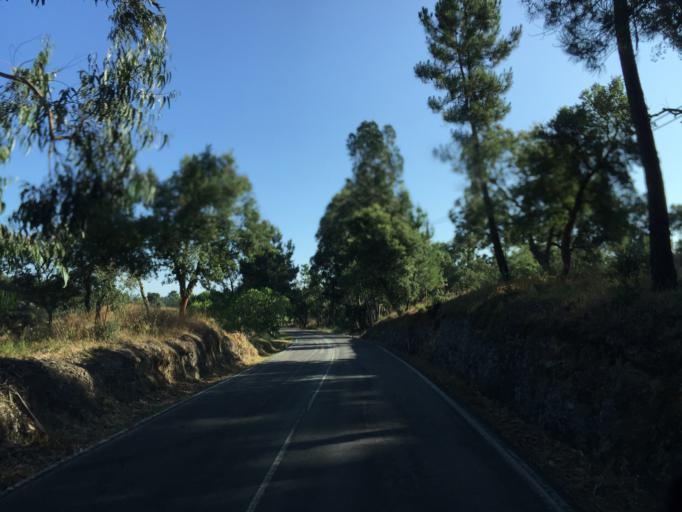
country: PT
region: Santarem
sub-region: Abrantes
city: Alferrarede
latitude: 39.5294
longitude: -8.1382
